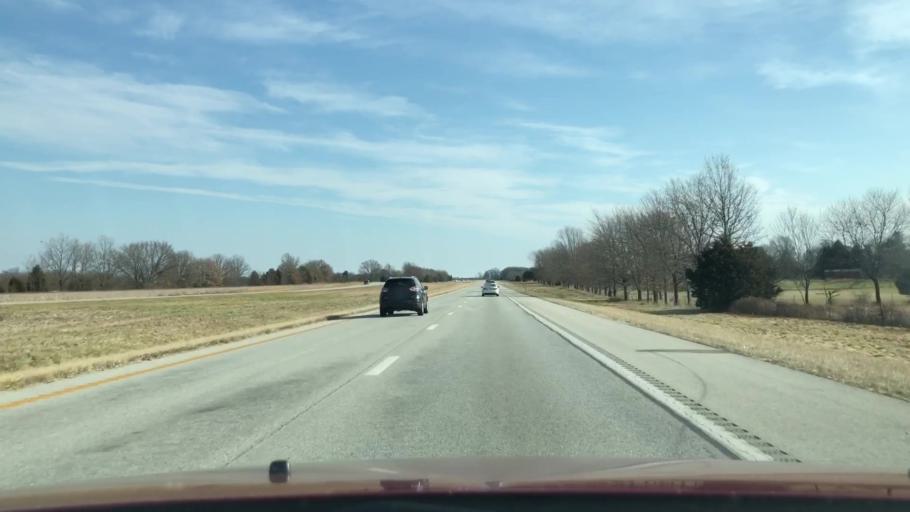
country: US
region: Missouri
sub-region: Webster County
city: Rogersville
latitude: 37.1229
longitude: -92.9945
